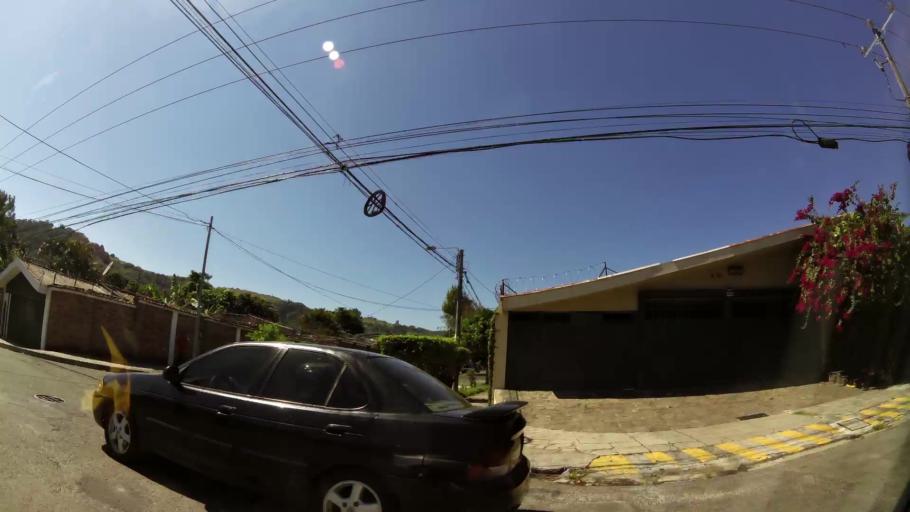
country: SV
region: La Libertad
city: Santa Tecla
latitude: 13.6697
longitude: -89.2814
